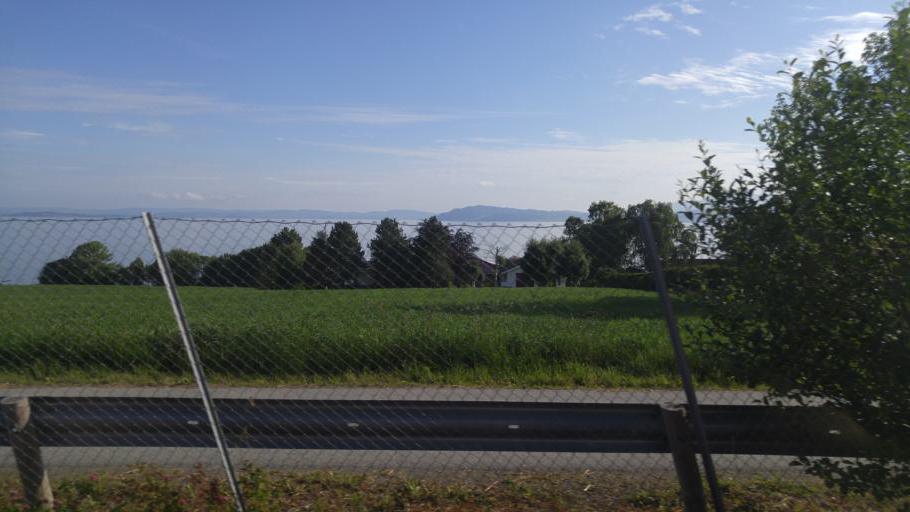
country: NO
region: Sor-Trondelag
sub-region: Malvik
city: Malvik
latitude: 63.4351
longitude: 10.6894
